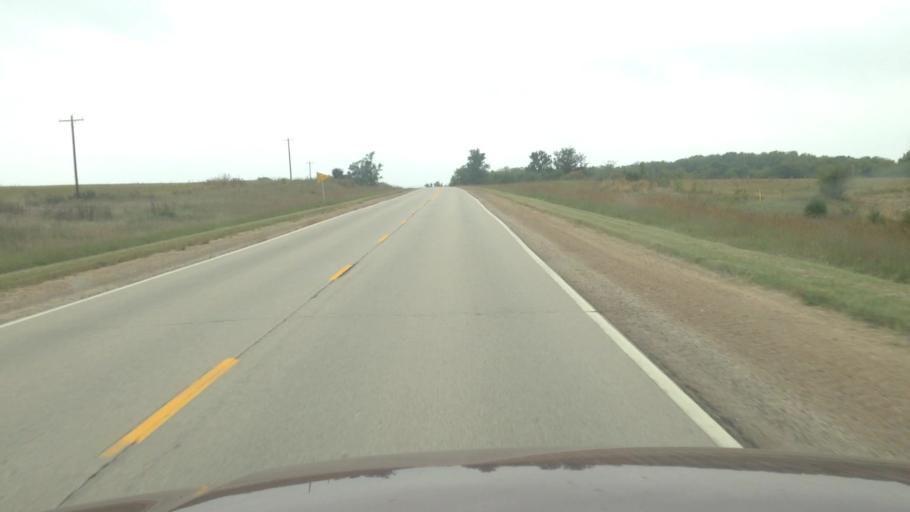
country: US
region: Kansas
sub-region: Jefferson County
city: Oskaloosa
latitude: 39.1201
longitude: -95.4837
